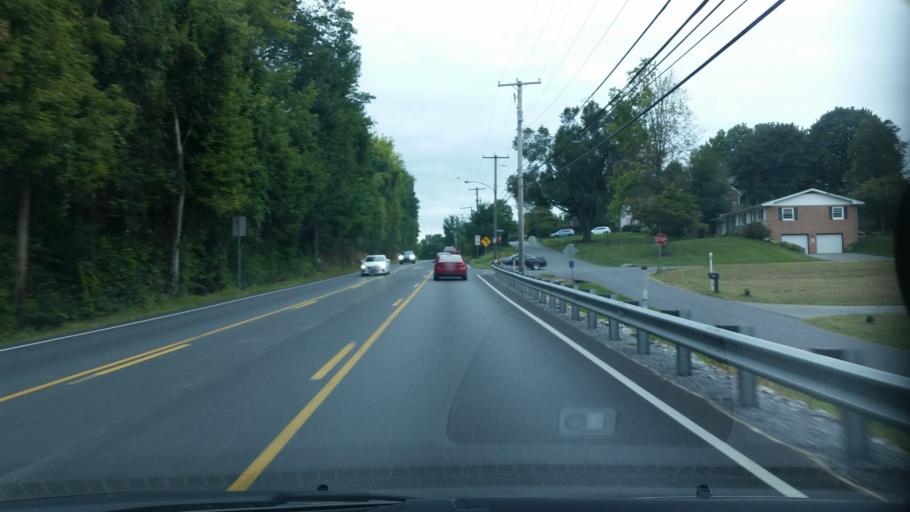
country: US
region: Pennsylvania
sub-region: Lancaster County
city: Lancaster
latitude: 40.0103
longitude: -76.2990
